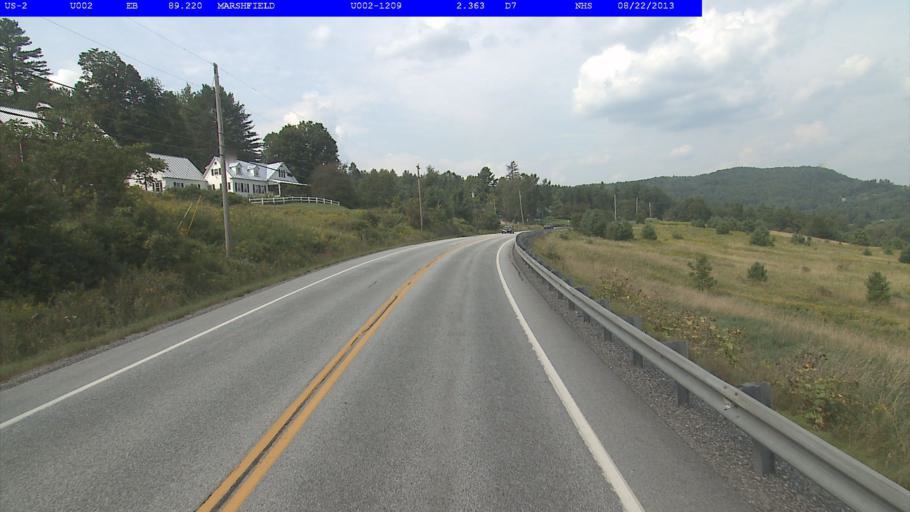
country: US
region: Vermont
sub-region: Washington County
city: Barre
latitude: 44.3049
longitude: -72.3993
